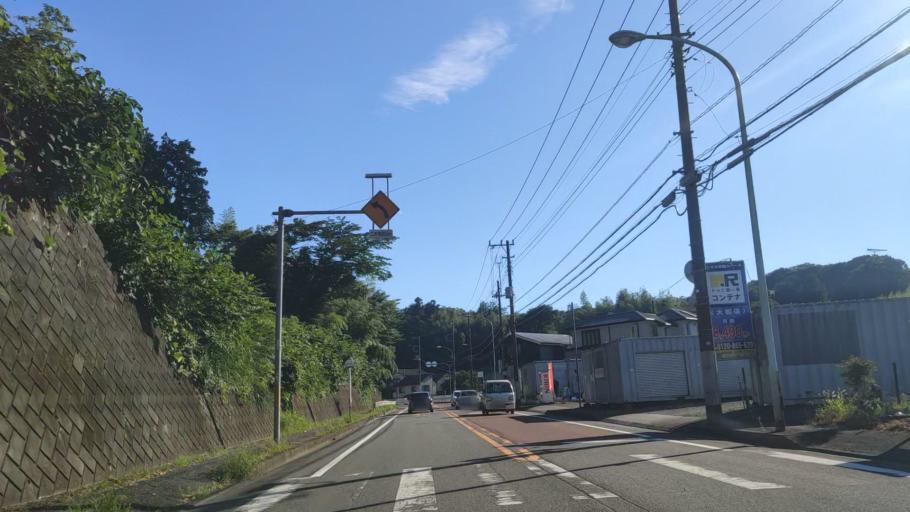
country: JP
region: Tokyo
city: Hachioji
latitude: 35.6231
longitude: 139.3147
